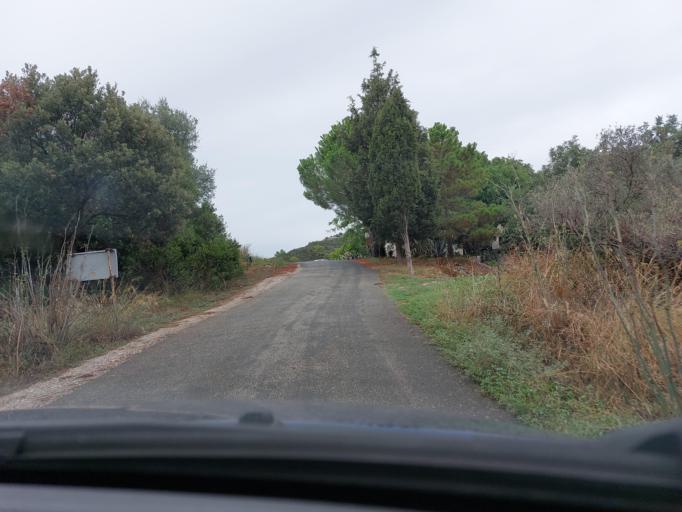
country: HR
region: Dubrovacko-Neretvanska
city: Smokvica
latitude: 42.7649
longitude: 16.9009
